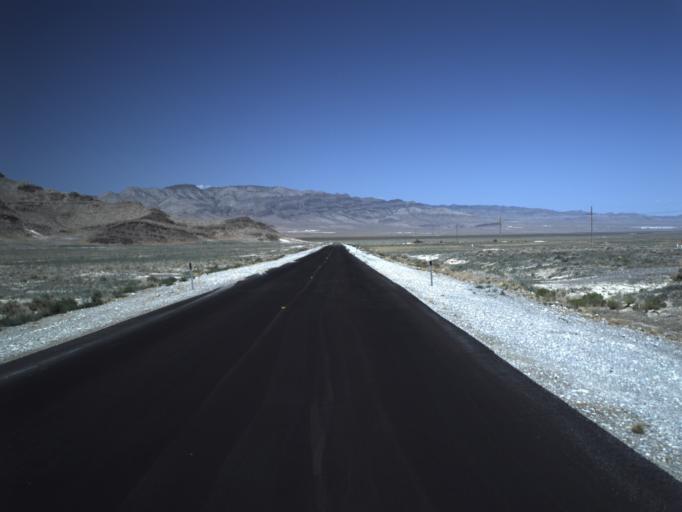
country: US
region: Utah
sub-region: Beaver County
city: Milford
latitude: 39.0563
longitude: -113.4303
